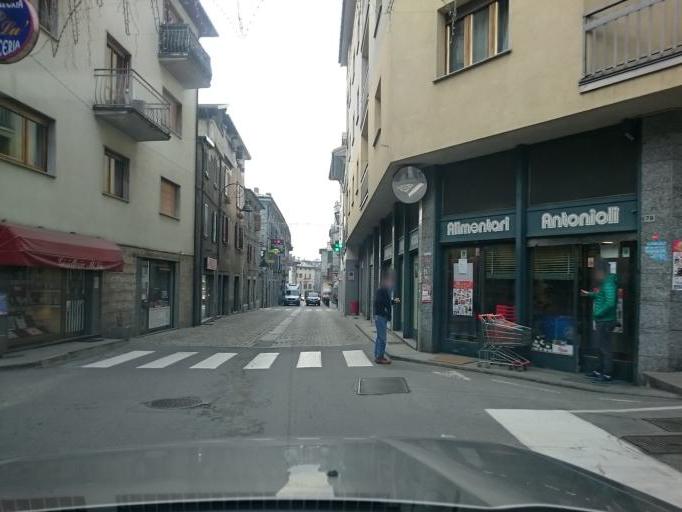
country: IT
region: Lombardy
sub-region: Provincia di Sondrio
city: Grosio
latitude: 46.2994
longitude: 10.2759
